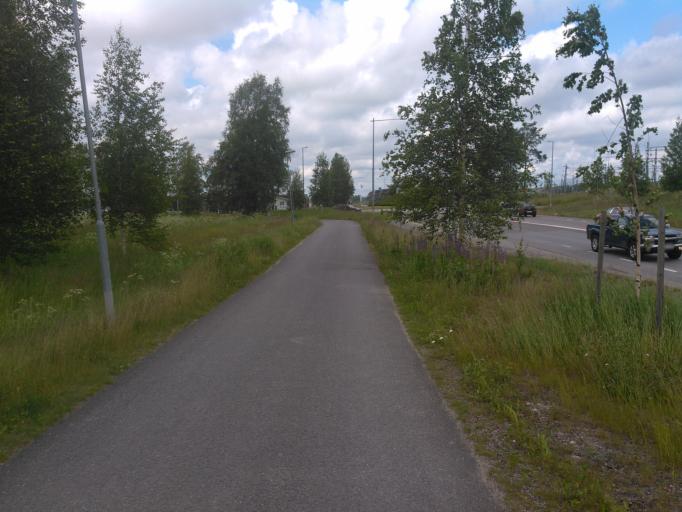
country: SE
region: Vaesterbotten
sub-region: Umea Kommun
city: Umea
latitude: 63.8404
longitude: 20.2421
